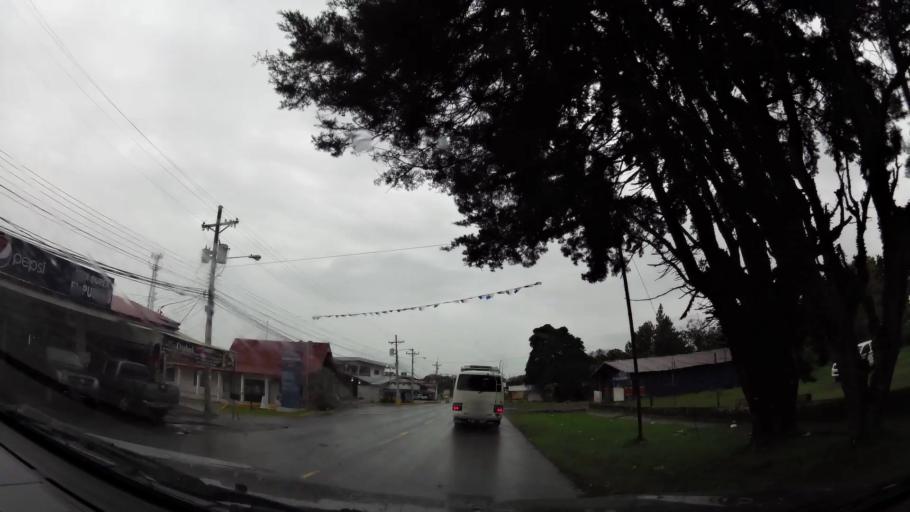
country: PA
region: Chiriqui
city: Volcan
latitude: 8.7790
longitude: -82.6427
